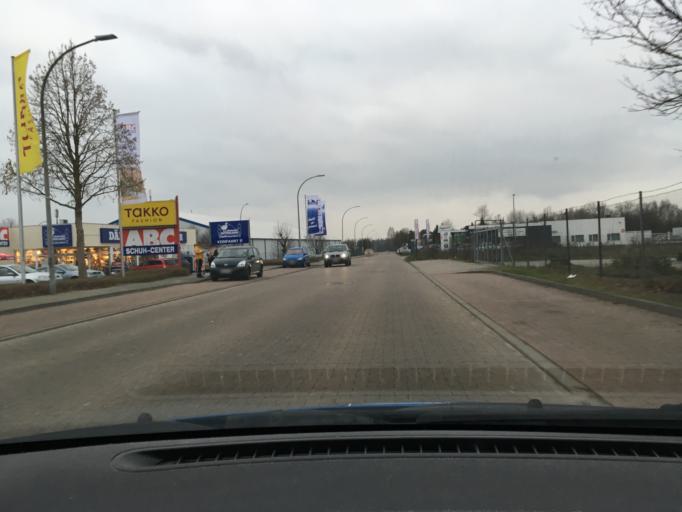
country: DE
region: Lower Saxony
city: Walsrode
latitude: 52.8651
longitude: 9.6184
